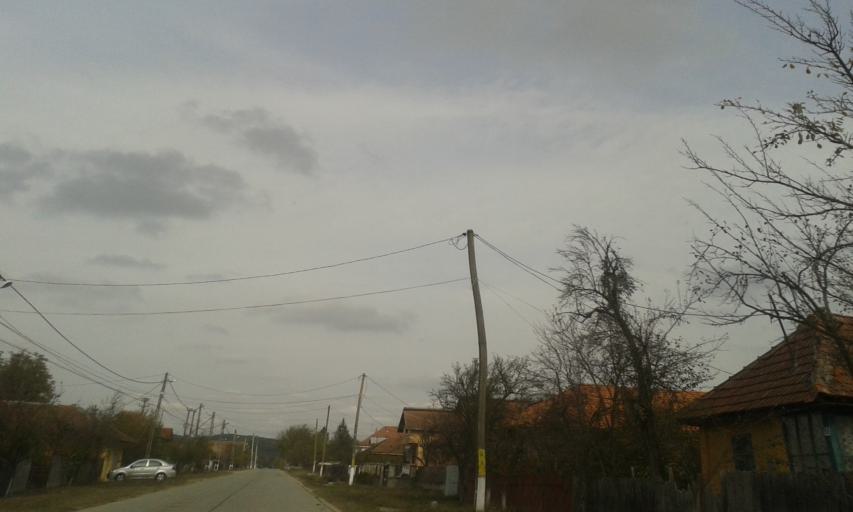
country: RO
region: Gorj
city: Logresti
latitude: 44.8719
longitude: 23.7057
